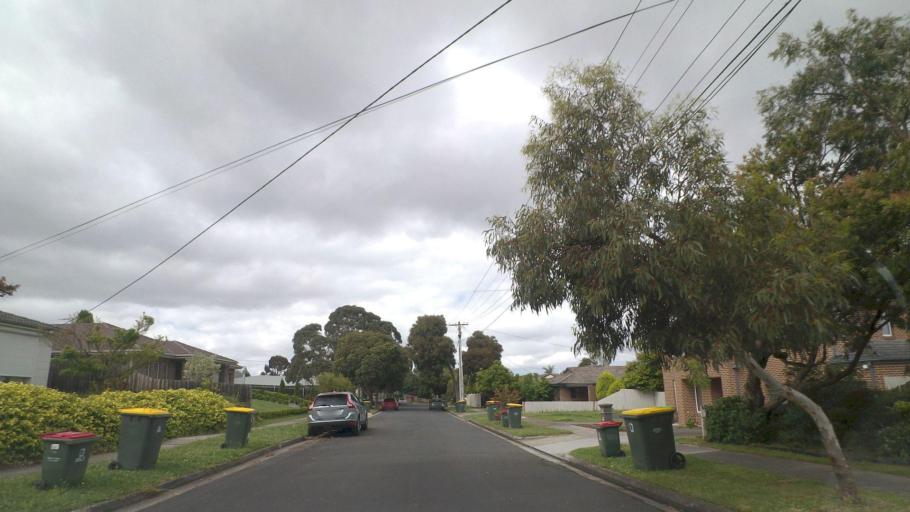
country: AU
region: Victoria
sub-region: Whitehorse
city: Vermont South
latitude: -37.8570
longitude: 145.1774
